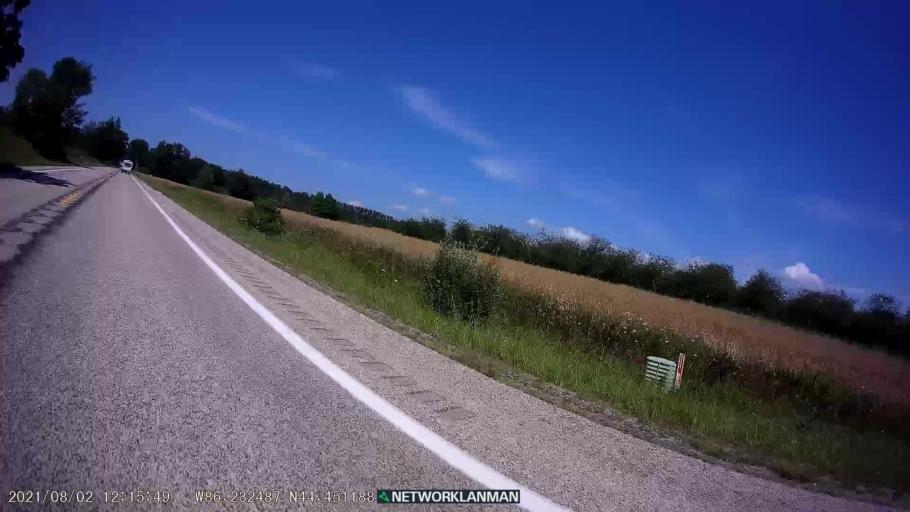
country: US
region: Michigan
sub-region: Benzie County
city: Frankfort
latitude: 44.4513
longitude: -86.2325
